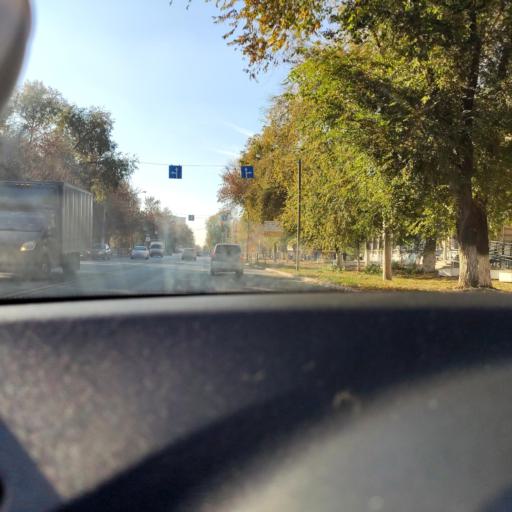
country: RU
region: Samara
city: Petra-Dubrava
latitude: 53.2225
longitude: 50.2743
